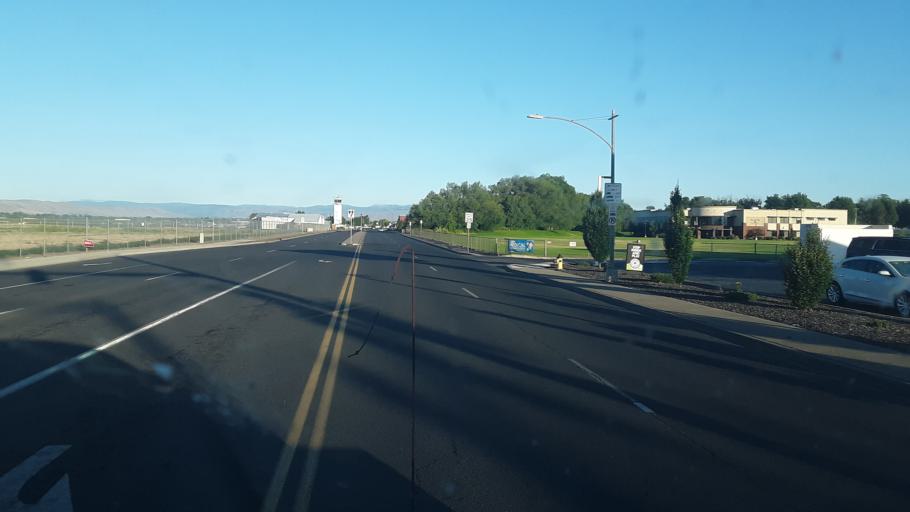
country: US
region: Washington
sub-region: Yakima County
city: Yakima
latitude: 46.5709
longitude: -120.5306
